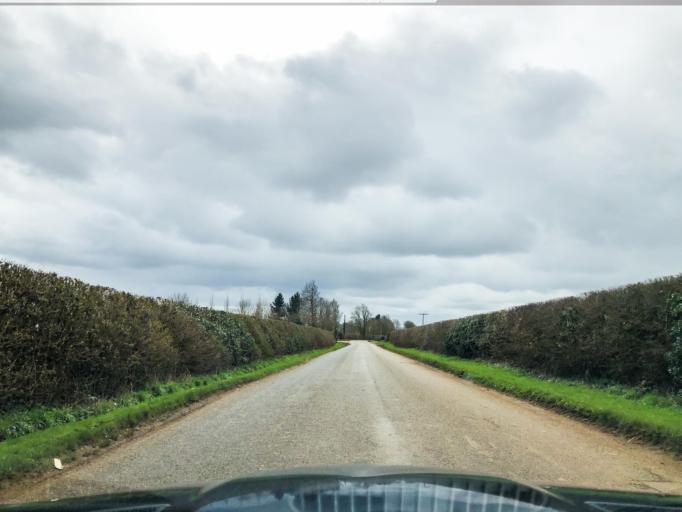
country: GB
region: England
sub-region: Oxfordshire
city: Hook Norton
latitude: 52.0951
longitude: -1.4798
